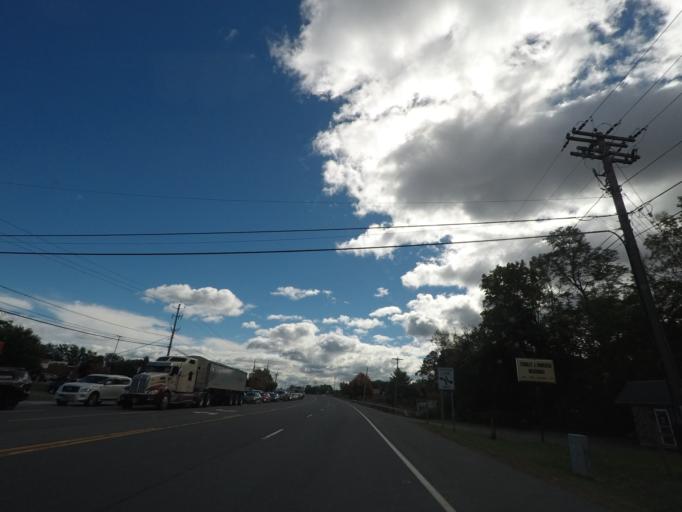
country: US
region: New York
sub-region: Saratoga County
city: Country Knolls
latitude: 42.8614
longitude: -73.7676
